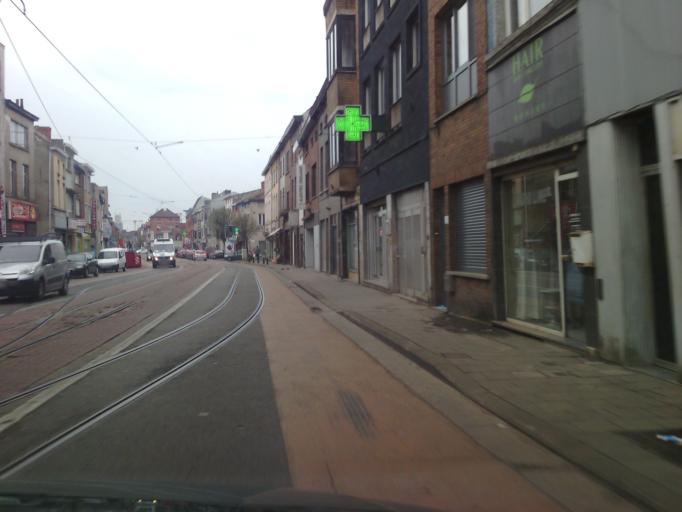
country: BE
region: Flanders
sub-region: Provincie Oost-Vlaanderen
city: Gent
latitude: 51.0698
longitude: 3.7299
